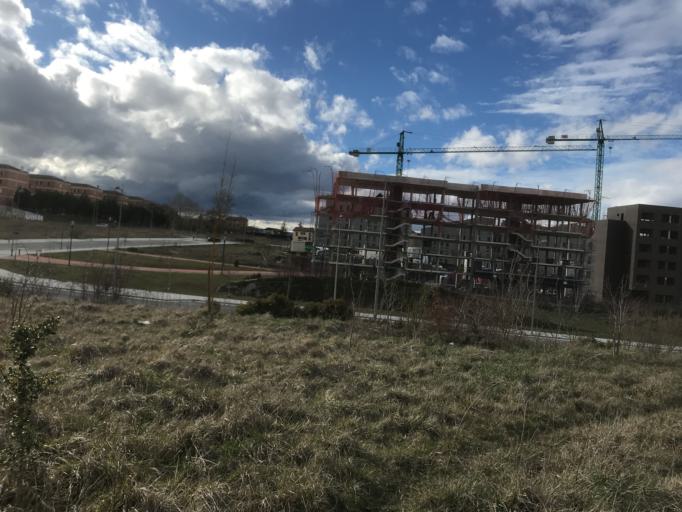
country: ES
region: Basque Country
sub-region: Provincia de Alava
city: Gasteiz / Vitoria
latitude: 42.8315
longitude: -2.6684
